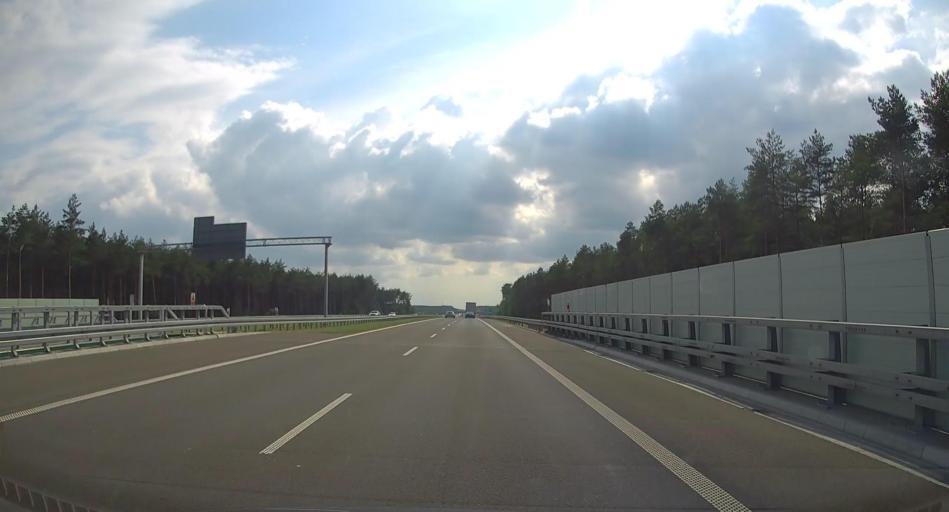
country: PL
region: Masovian Voivodeship
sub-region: Powiat wyszkowski
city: Branszczyk
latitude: 52.6917
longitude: 21.6443
